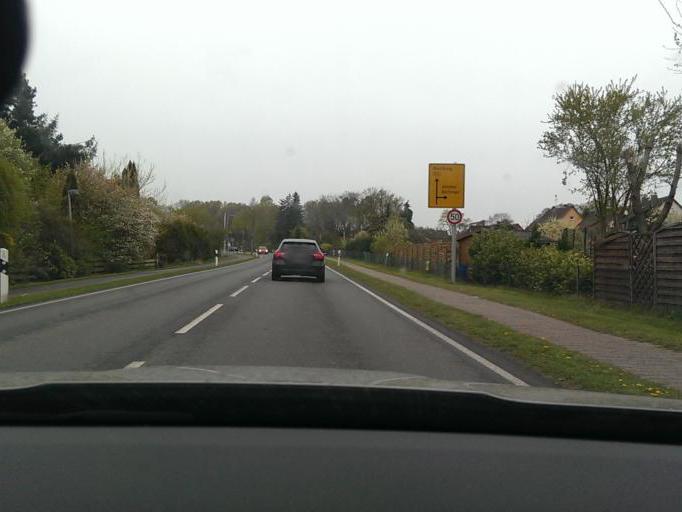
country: DE
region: Lower Saxony
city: Schwarmstedt
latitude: 52.6843
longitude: 9.6098
